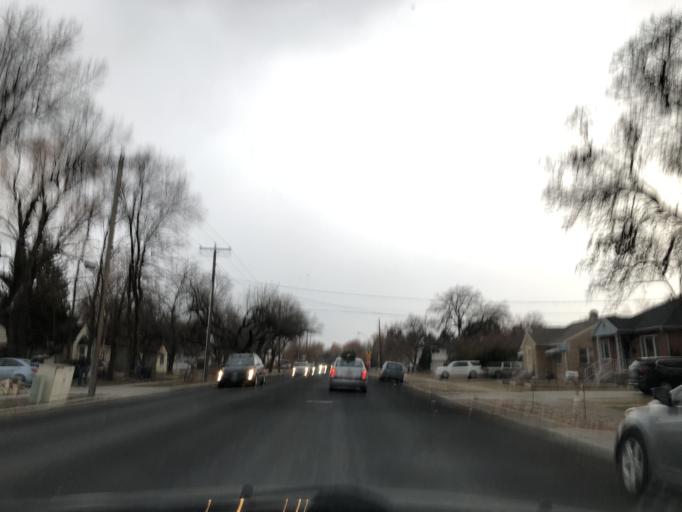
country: US
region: Utah
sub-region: Cache County
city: Logan
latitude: 41.7457
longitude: -111.8295
